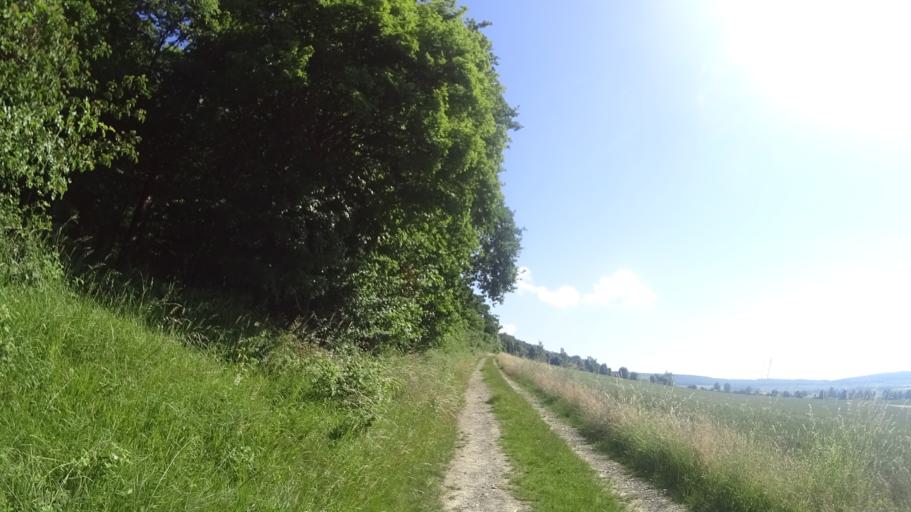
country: DE
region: Lower Saxony
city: Baddeckenstedt
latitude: 52.0946
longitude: 10.2574
